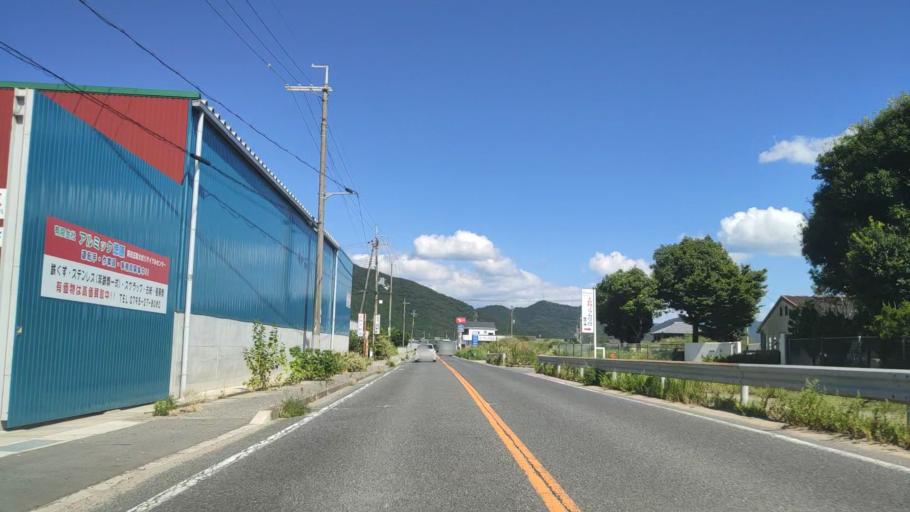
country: JP
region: Hyogo
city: Nishiwaki
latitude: 35.0396
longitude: 134.9842
